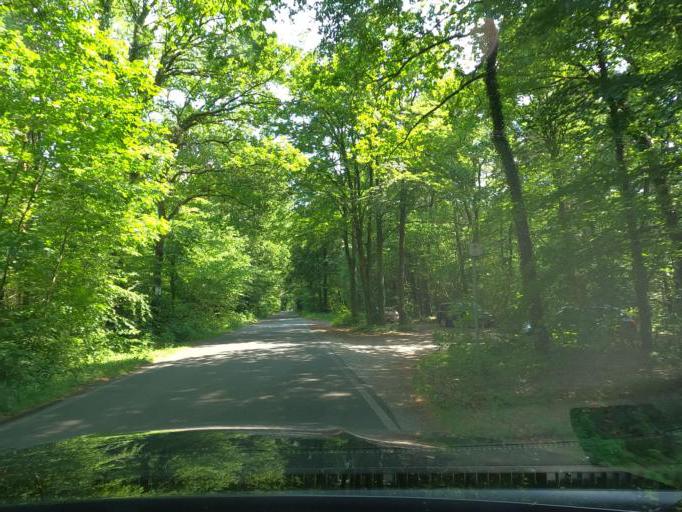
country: DE
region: Lower Saxony
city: Isernhagen Farster Bauerschaft
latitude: 52.4074
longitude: 9.8526
